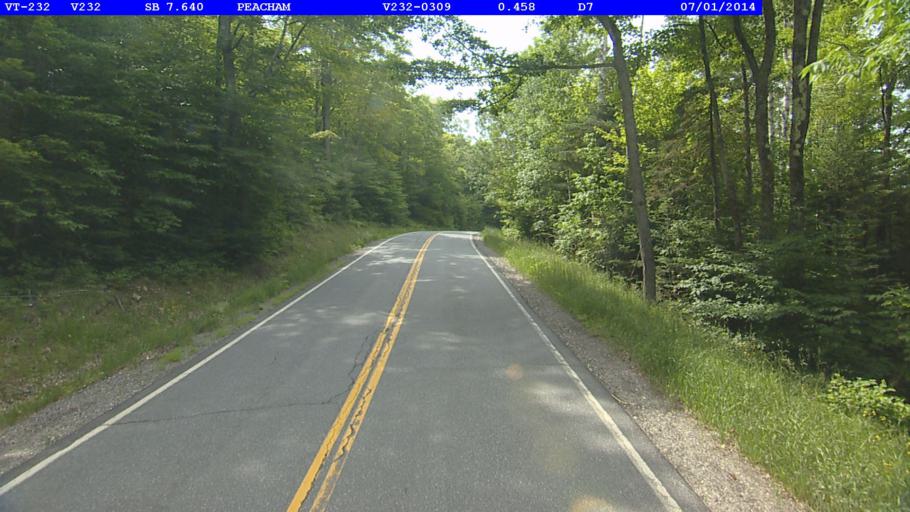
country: US
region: Vermont
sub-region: Caledonia County
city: Hardwick
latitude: 44.3022
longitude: -72.3014
